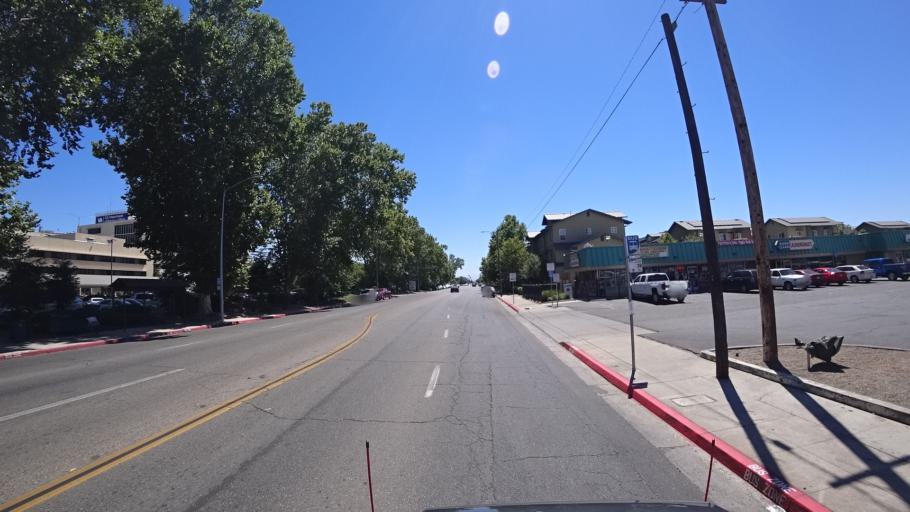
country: US
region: California
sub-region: Fresno County
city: Fresno
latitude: 36.7722
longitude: -119.7811
